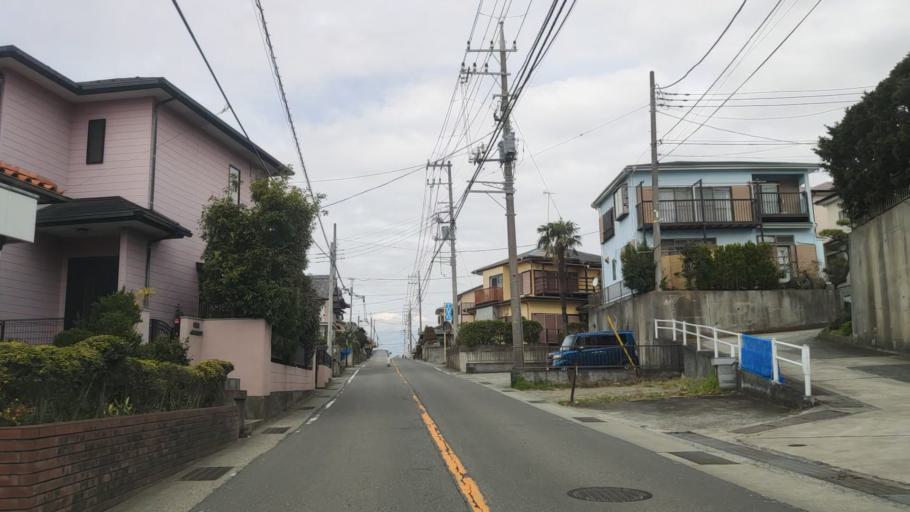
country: JP
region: Kanagawa
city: Ninomiya
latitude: 35.2939
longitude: 139.2336
